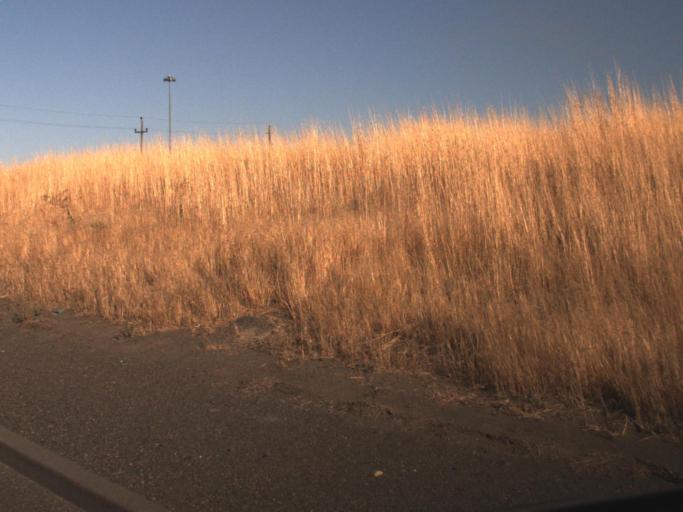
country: US
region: Washington
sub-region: Franklin County
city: Pasco
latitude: 46.2218
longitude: -119.0782
